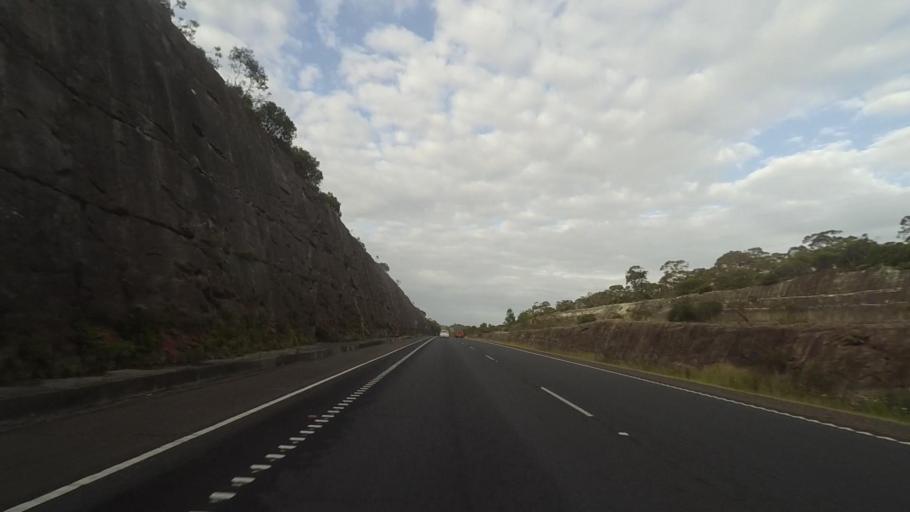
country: AU
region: New South Wales
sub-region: Wollongong
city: Helensburgh
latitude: -34.2216
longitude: 150.9524
